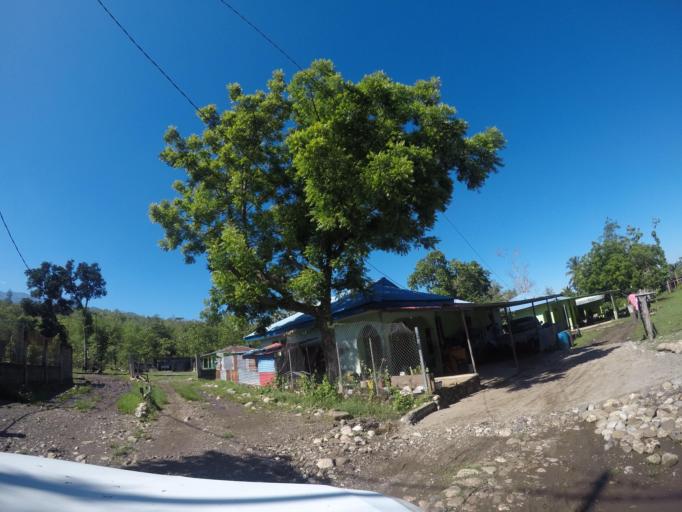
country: TL
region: Bobonaro
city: Maliana
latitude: -8.9927
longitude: 125.2130
